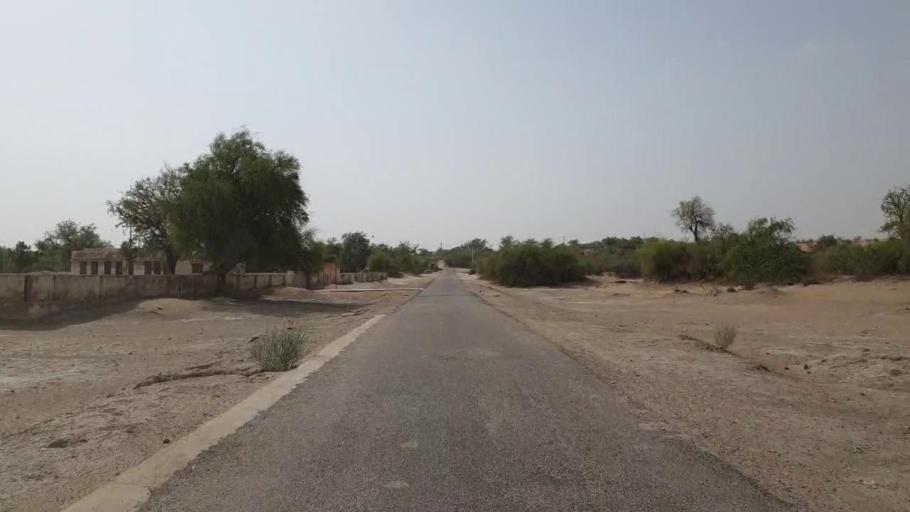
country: PK
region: Sindh
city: Mithi
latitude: 24.5743
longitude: 69.9298
